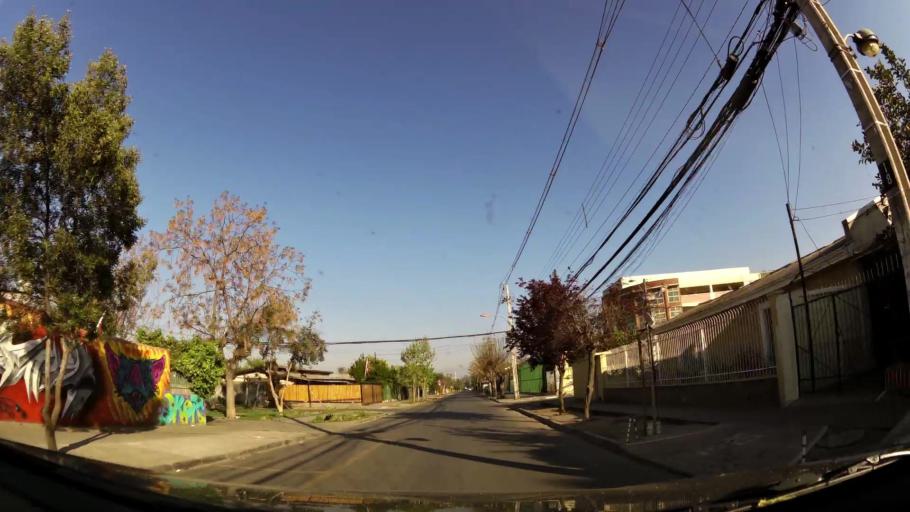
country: CL
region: Santiago Metropolitan
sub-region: Provincia de Santiago
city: Santiago
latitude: -33.3746
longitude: -70.6406
